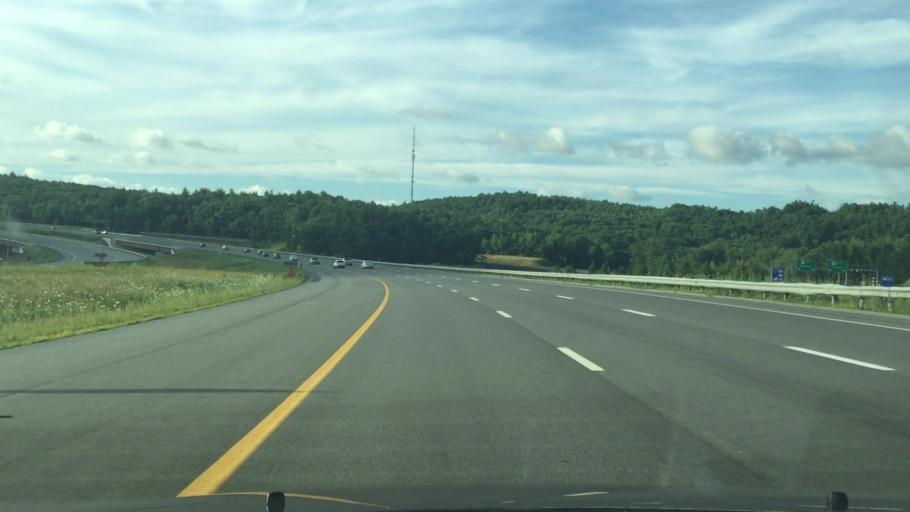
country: US
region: New Hampshire
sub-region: Rockingham County
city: Windham
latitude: 42.8050
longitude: -71.2706
